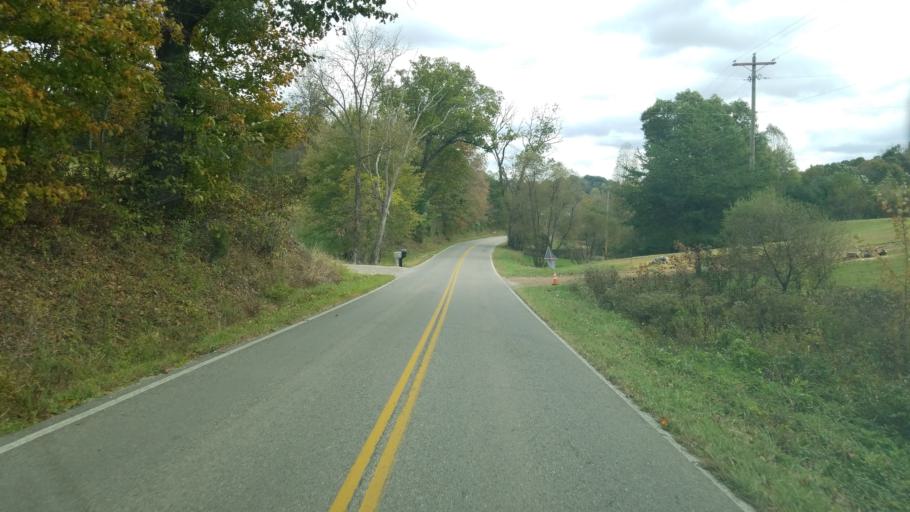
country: US
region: Ohio
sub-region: Jackson County
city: Jackson
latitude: 39.1237
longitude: -82.6290
